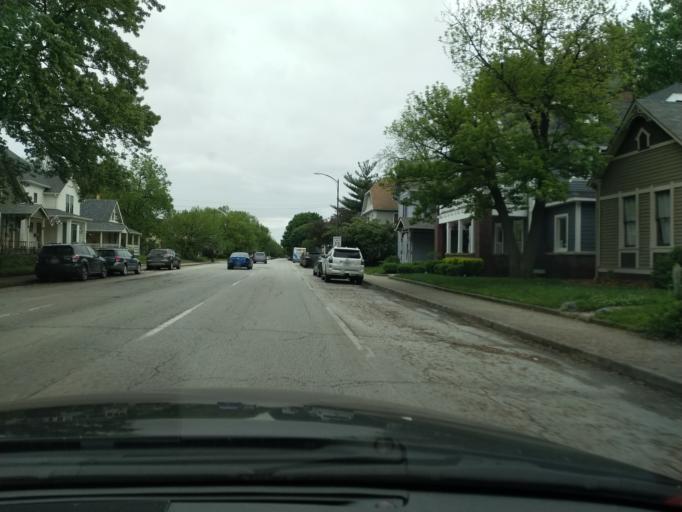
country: US
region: Indiana
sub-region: Marion County
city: Indianapolis
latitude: 39.7893
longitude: -86.1537
